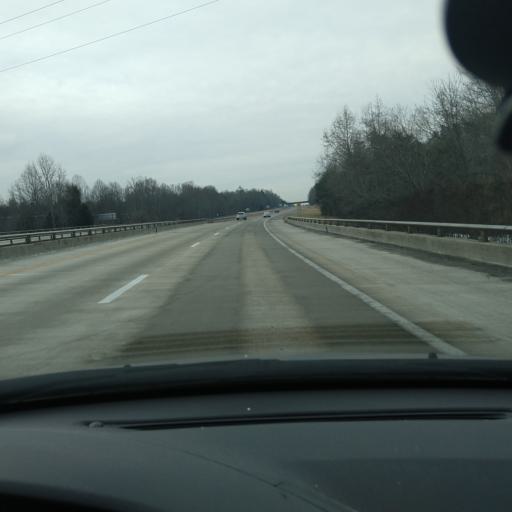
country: US
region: North Carolina
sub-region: Davidson County
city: Midway
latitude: 36.0155
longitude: -80.2355
